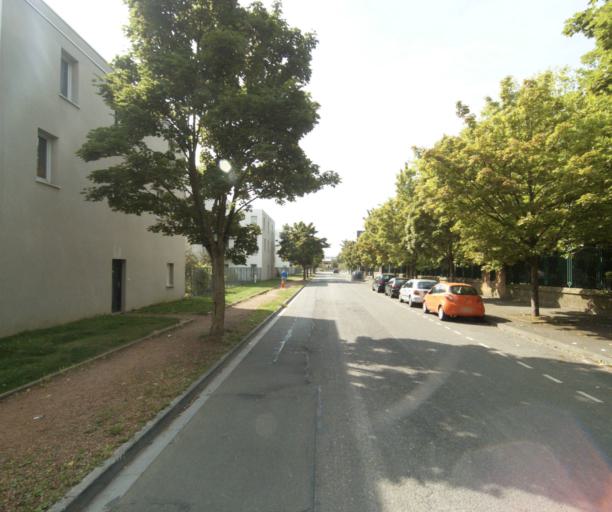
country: FR
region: Nord-Pas-de-Calais
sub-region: Departement du Nord
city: Wattignies
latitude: 50.6067
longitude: 3.0537
